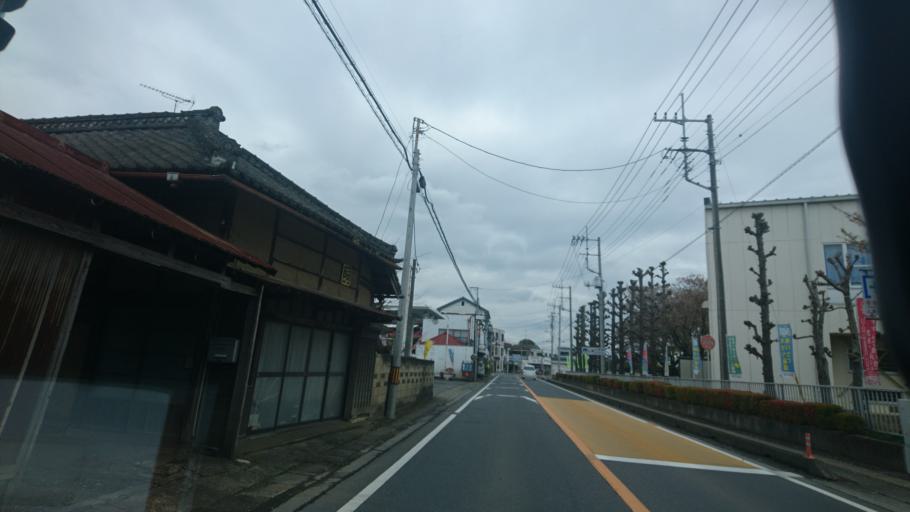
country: JP
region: Ibaraki
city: Shimodate
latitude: 36.2178
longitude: 139.9349
